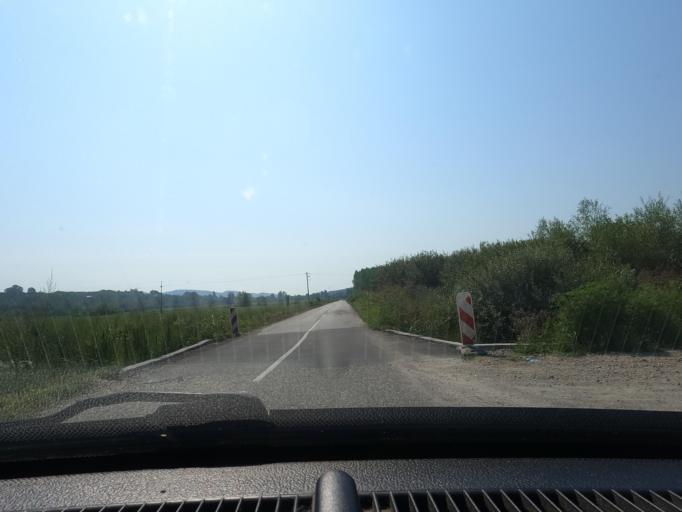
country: RS
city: Lipnicki Sor
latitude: 44.5763
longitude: 19.2744
